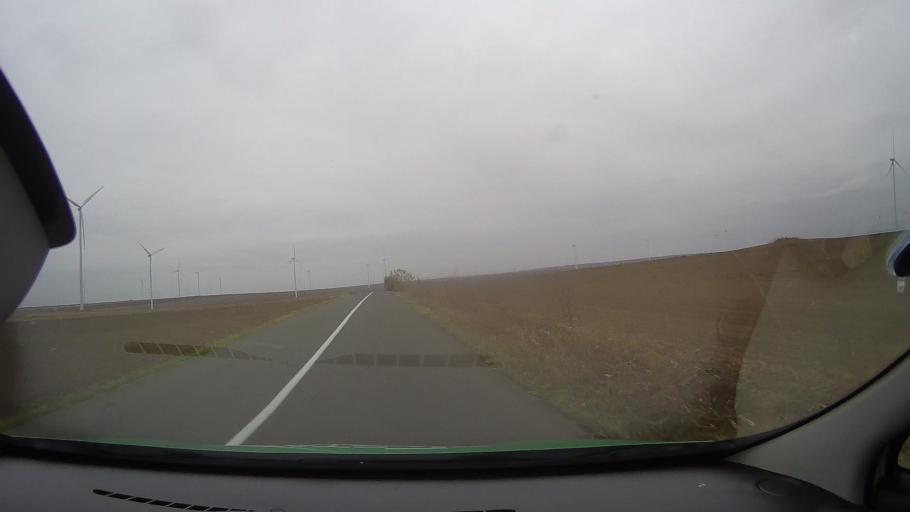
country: RO
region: Constanta
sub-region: Comuna Pantelimon
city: Pantelimon
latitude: 44.5094
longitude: 28.3409
